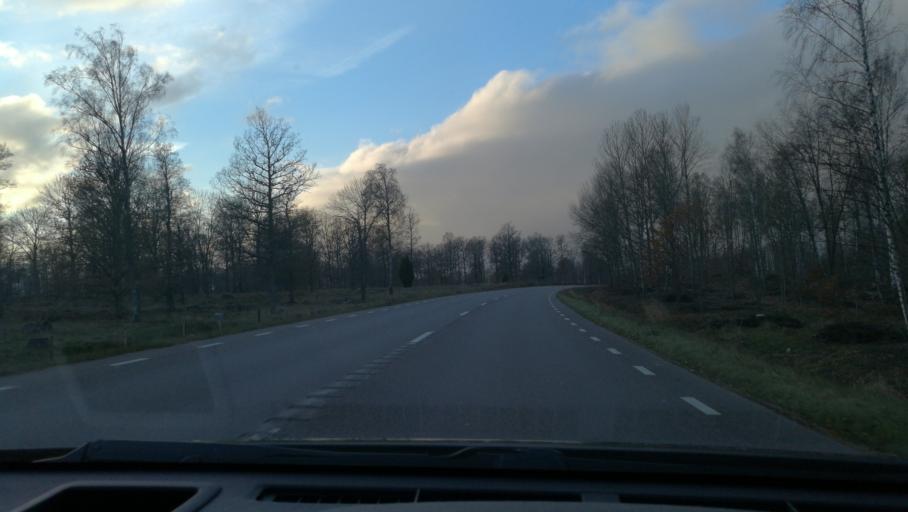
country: SE
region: Soedermanland
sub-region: Vingakers Kommun
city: Vingaker
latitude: 59.1487
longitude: 16.0556
